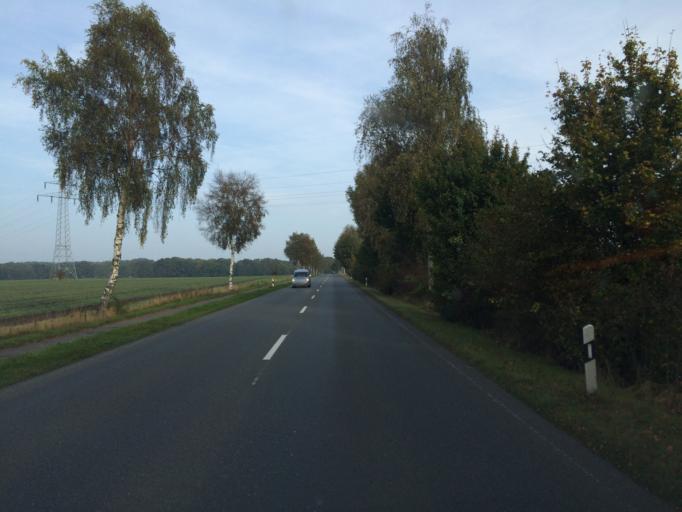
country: DE
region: Lower Saxony
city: Soltau
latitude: 52.9925
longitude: 9.9056
